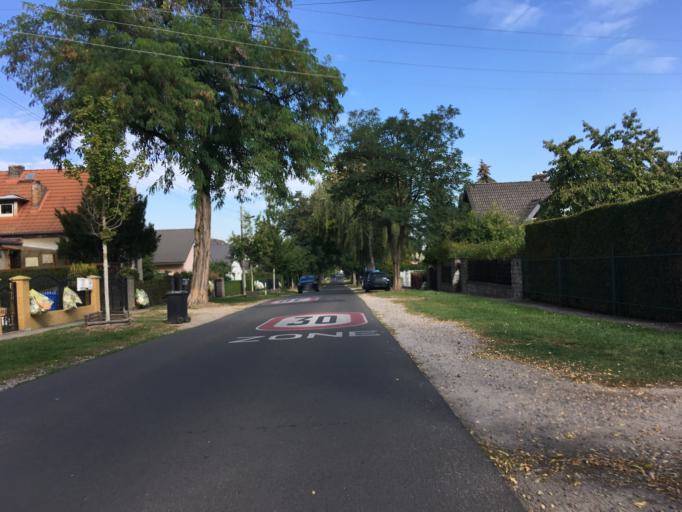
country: DE
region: Berlin
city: Kaulsdorf
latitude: 52.5255
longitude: 13.5981
